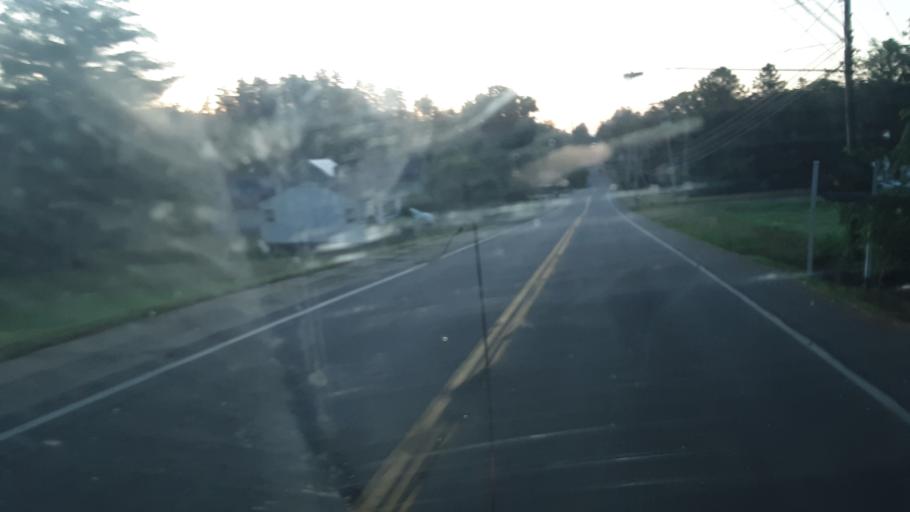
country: US
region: New York
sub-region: Saratoga County
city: Ballston Spa
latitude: 42.9999
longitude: -73.8610
